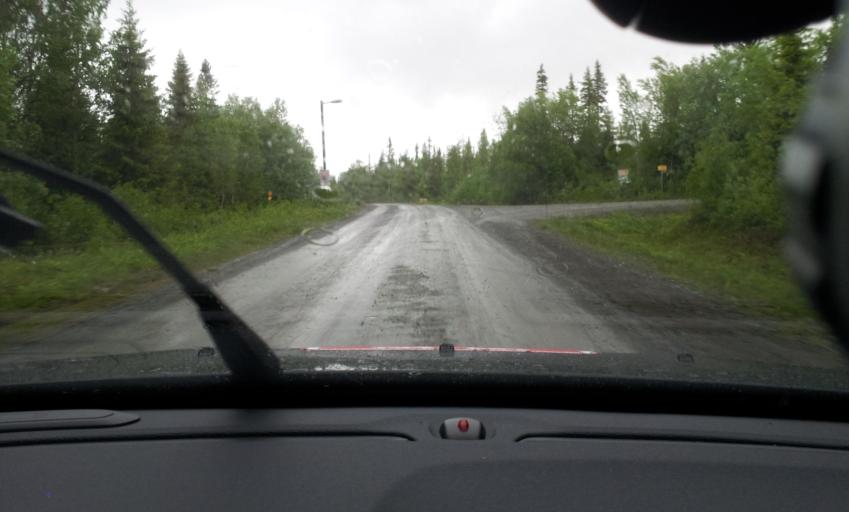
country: SE
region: Jaemtland
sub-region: Are Kommun
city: Are
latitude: 63.2180
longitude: 13.0710
